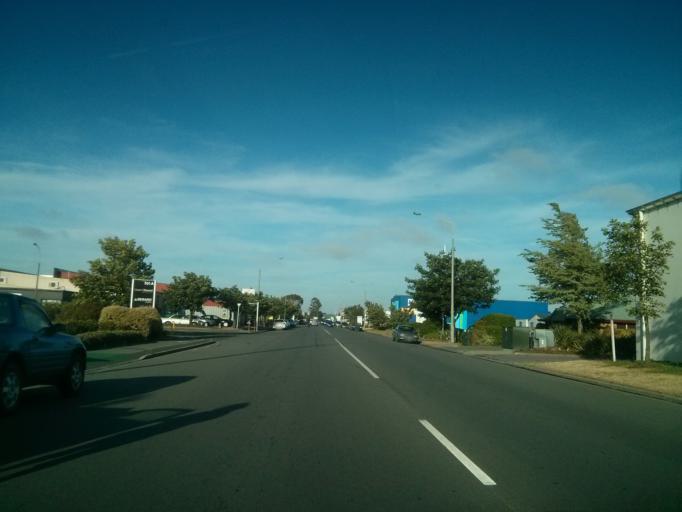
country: NZ
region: Canterbury
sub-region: Selwyn District
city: Prebbleton
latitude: -43.5380
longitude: 172.5362
